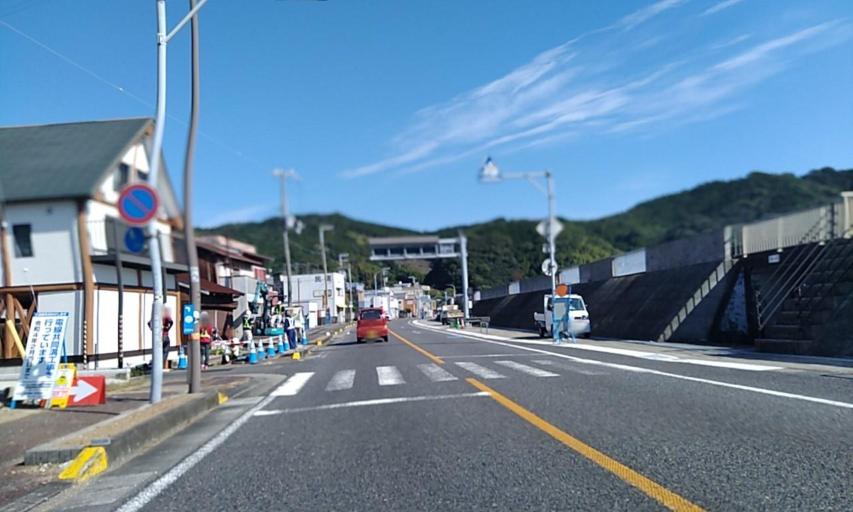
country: JP
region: Wakayama
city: Shingu
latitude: 33.8895
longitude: 136.1040
